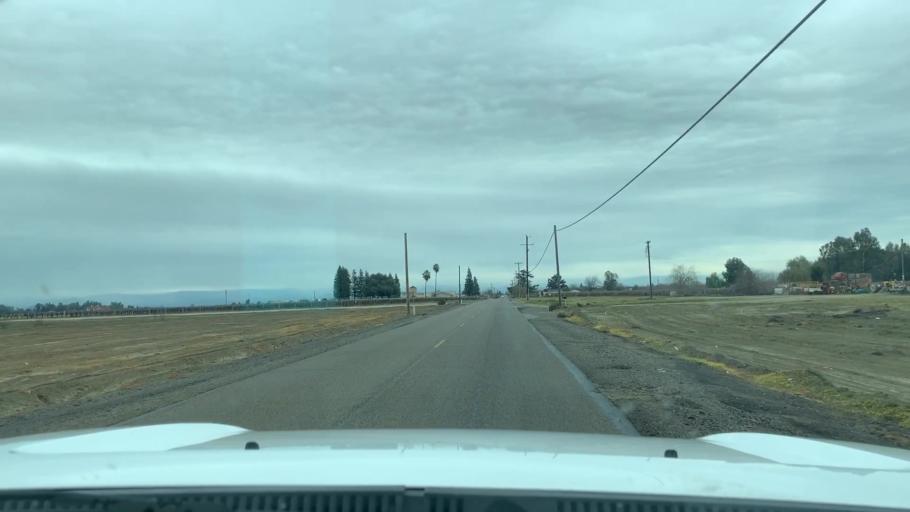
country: US
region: California
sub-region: Fresno County
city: Caruthers
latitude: 36.5473
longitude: -119.7337
